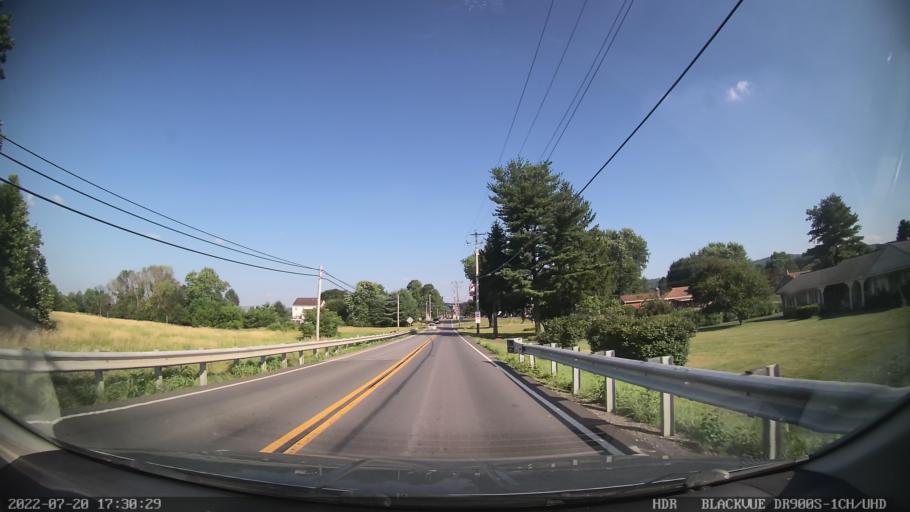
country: US
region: Pennsylvania
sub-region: Berks County
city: Blandon
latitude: 40.4470
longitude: -75.8962
